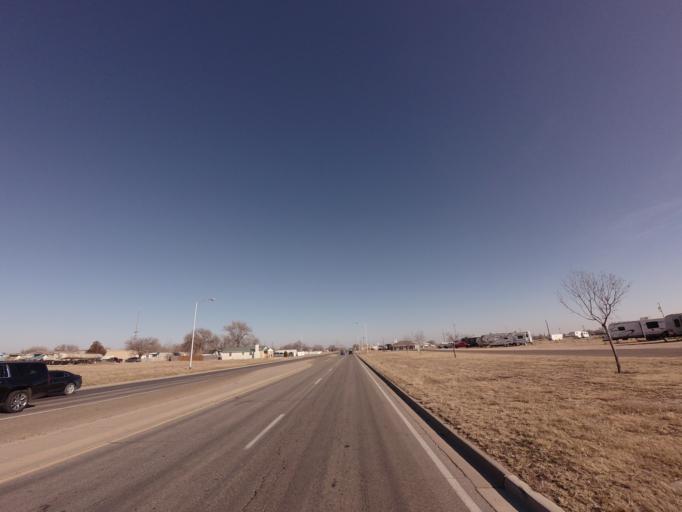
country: US
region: New Mexico
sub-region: Curry County
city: Clovis
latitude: 34.4007
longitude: -103.2364
